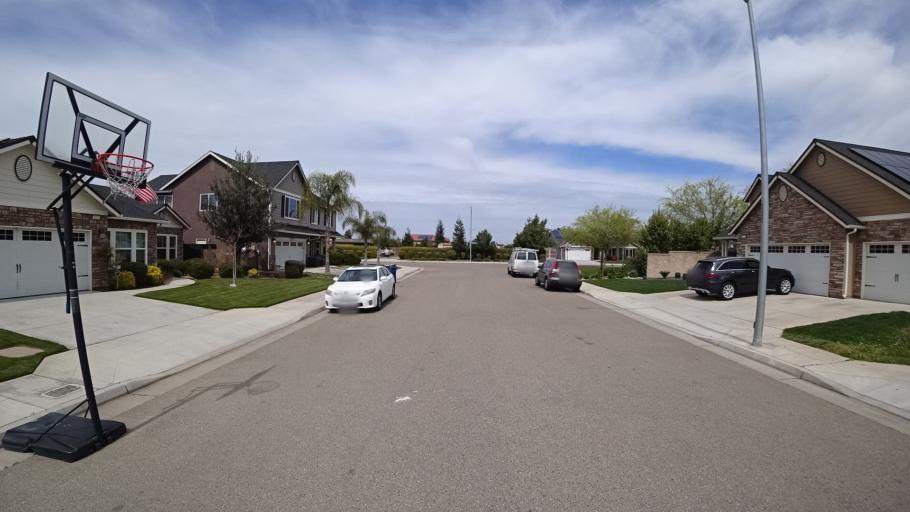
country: US
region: California
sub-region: Fresno County
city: Biola
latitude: 36.8139
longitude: -119.9250
